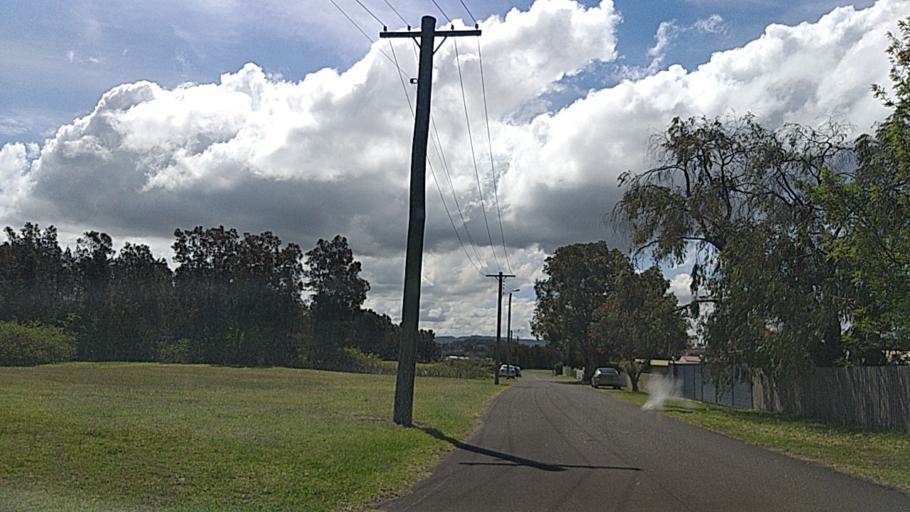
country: AU
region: New South Wales
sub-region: Wollongong
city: Lake Heights
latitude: -34.5031
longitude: 150.8742
